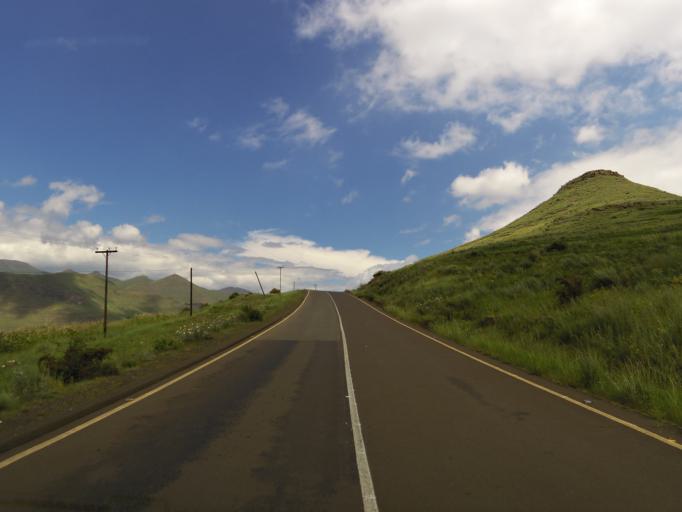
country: LS
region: Thaba-Tseka
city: Thaba-Tseka
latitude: -29.1320
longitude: 28.4930
